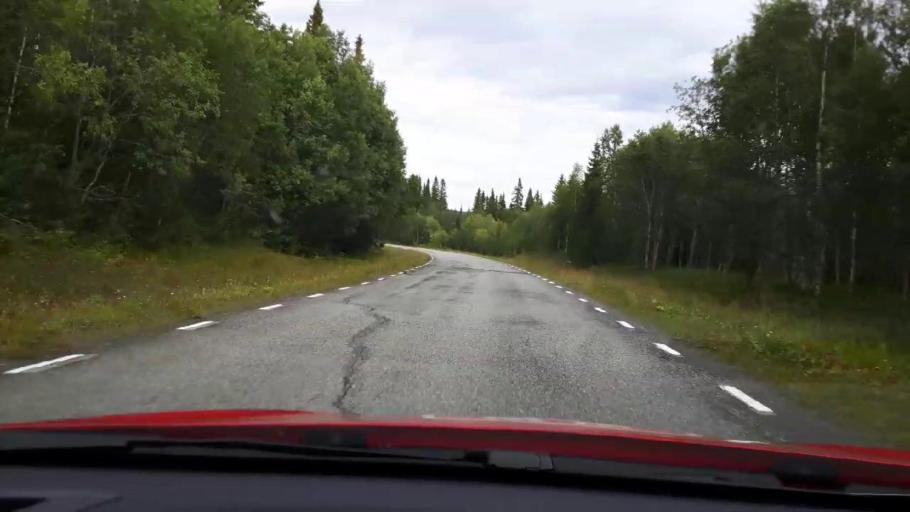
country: SE
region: Jaemtland
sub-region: Are Kommun
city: Are
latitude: 63.7167
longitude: 12.9662
